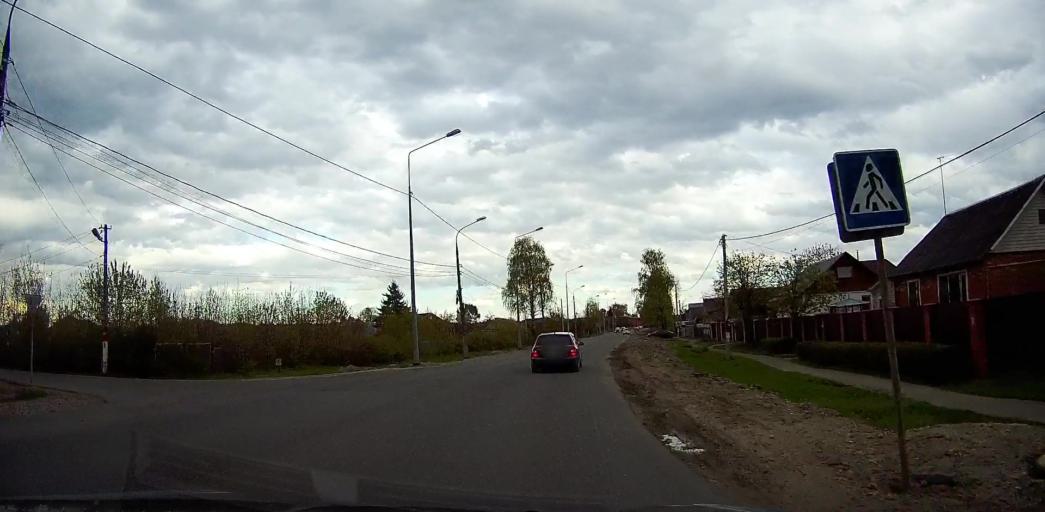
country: RU
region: Moskovskaya
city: Pavlovskiy Posad
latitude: 55.7716
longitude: 38.6914
